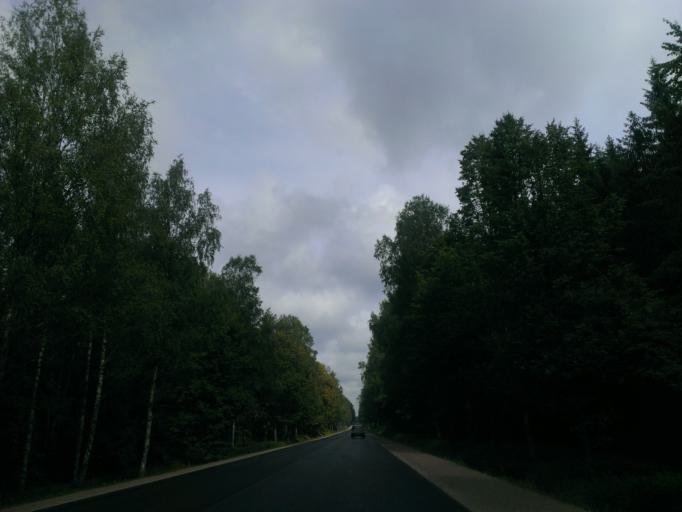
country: LV
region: Amatas Novads
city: Drabesi
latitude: 57.2145
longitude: 25.1841
